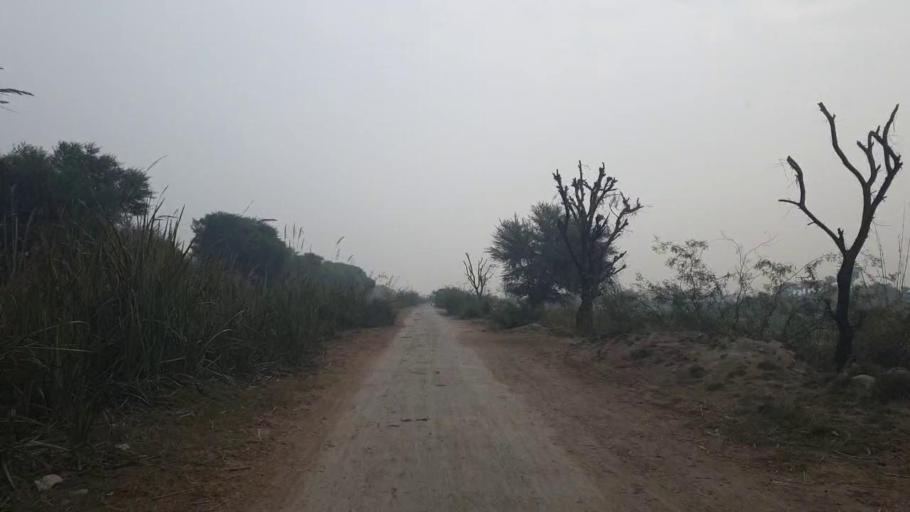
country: PK
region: Sindh
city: Tando Adam
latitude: 25.7521
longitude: 68.7000
